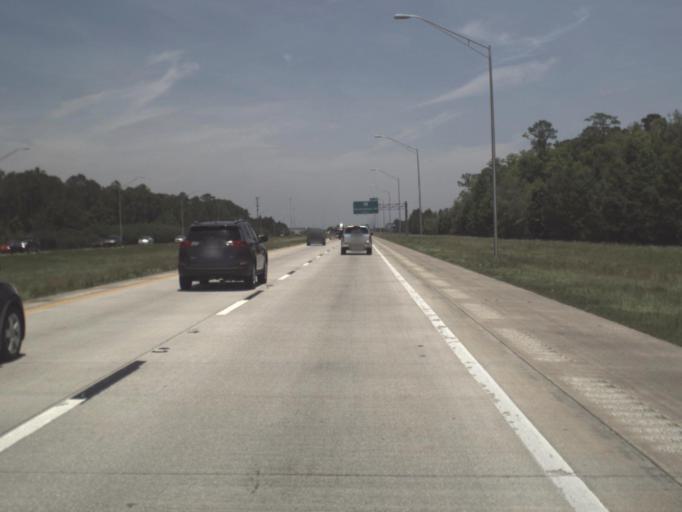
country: US
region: Florida
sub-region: Saint Johns County
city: Palm Valley
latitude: 30.2021
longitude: -81.5136
